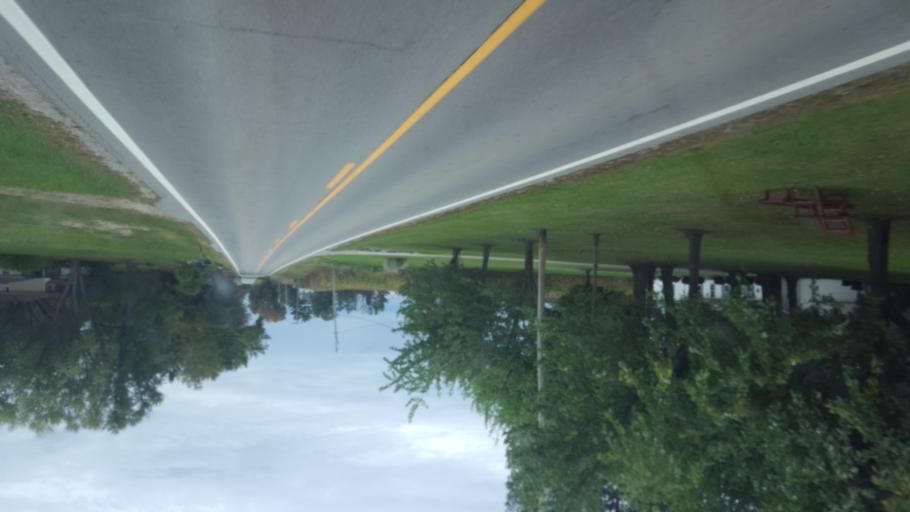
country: US
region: Ohio
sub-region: Huron County
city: Wakeman
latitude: 41.2689
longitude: -82.3956
